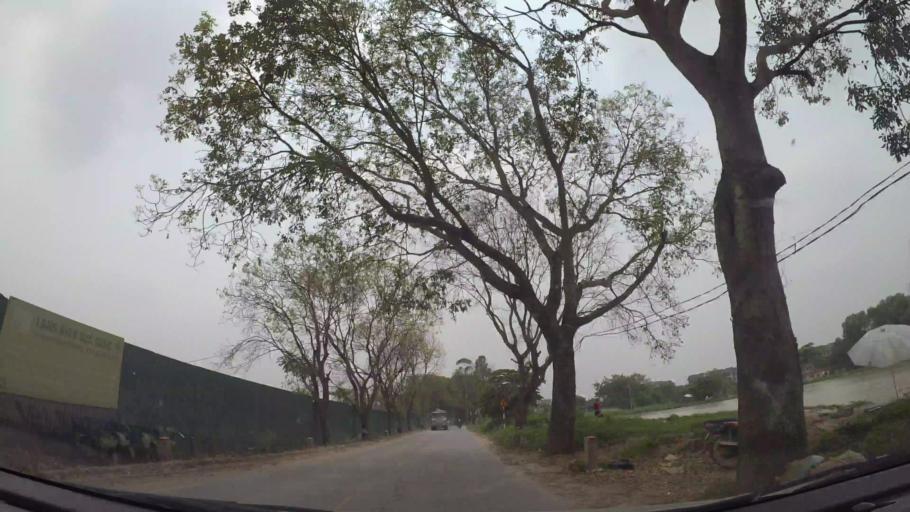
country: VN
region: Ha Noi
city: Cau Dien
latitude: 21.0217
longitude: 105.7432
